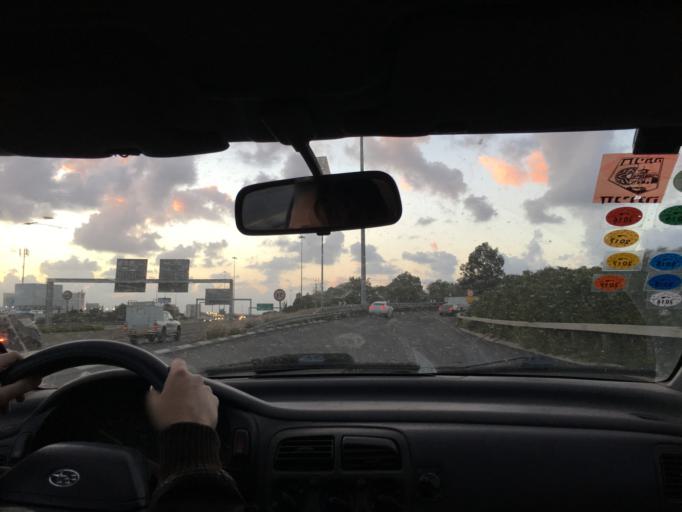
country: IL
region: Tel Aviv
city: Herzliyya
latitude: 32.1403
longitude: 34.8085
